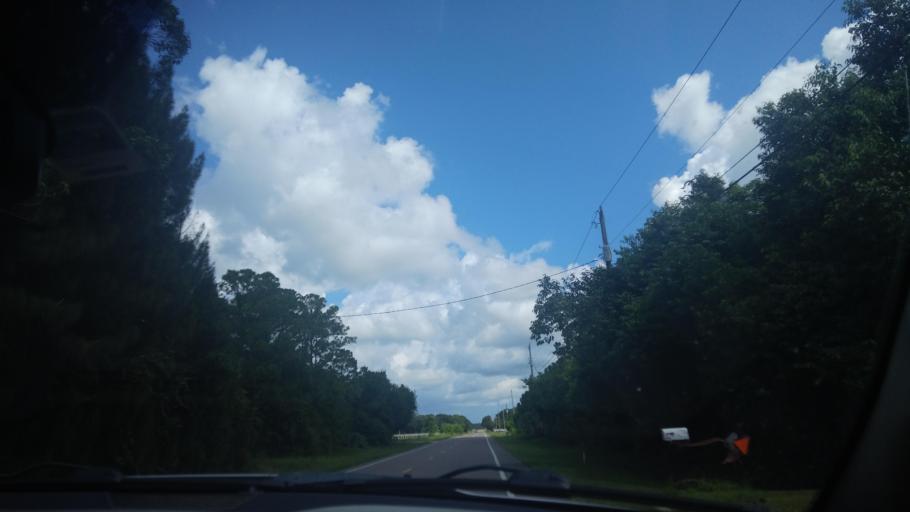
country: US
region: Florida
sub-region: Indian River County
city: Fellsmere
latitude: 27.8144
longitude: -80.6072
